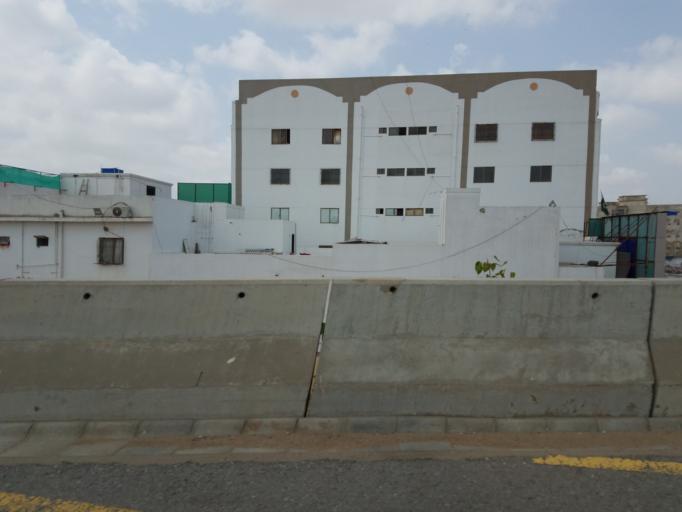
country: PK
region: Sindh
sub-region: Karachi District
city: Karachi
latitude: 24.9165
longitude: 67.0783
